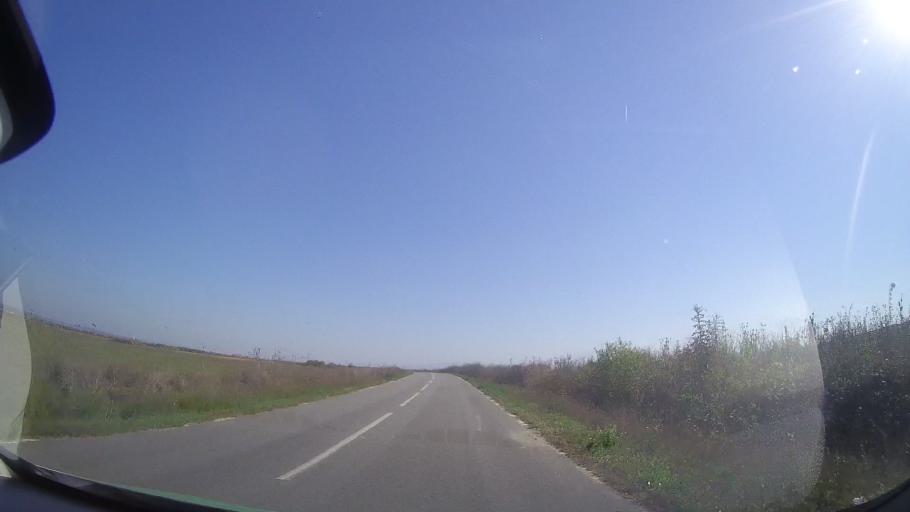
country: RO
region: Timis
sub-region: Comuna Bethausen
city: Bethausen
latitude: 45.7939
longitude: 21.9737
